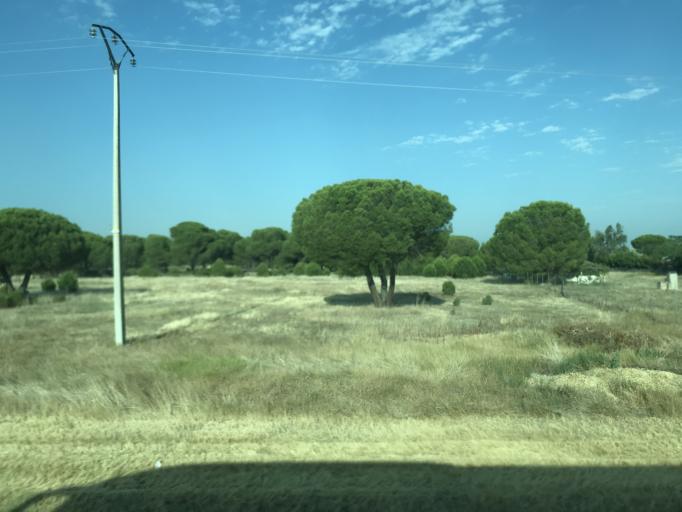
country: ES
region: Castille and Leon
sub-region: Provincia de Valladolid
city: La Pedraja de Portillo
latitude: 41.4938
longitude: -4.6840
